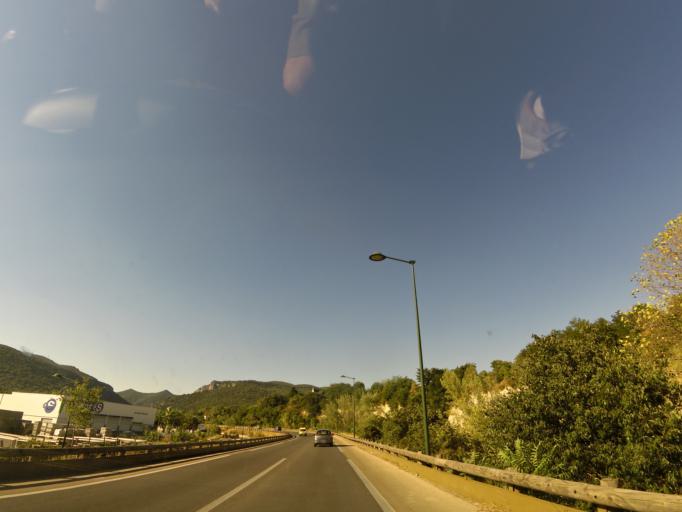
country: FR
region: Languedoc-Roussillon
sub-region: Departement de l'Herault
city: Ganges
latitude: 43.9336
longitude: 3.7130
